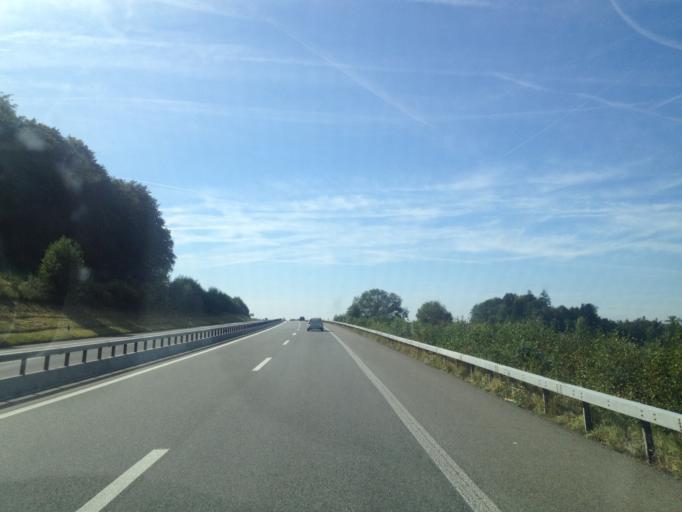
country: CH
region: Fribourg
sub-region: Sense District
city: Dudingen
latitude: 46.8663
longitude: 7.2115
